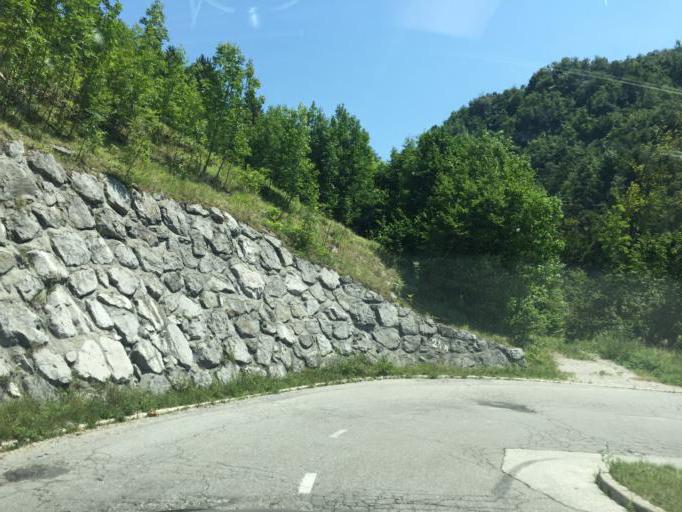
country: SI
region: Idrija
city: Spodnja Idrija
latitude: 46.0308
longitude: 14.0433
